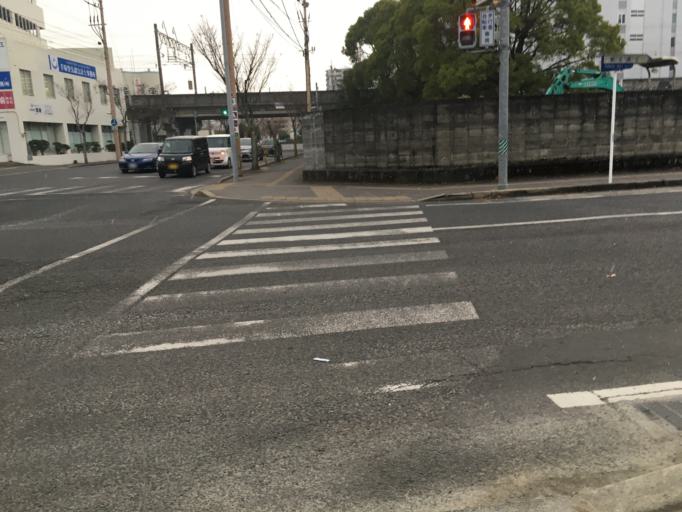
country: JP
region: Saga Prefecture
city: Saga-shi
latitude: 33.2658
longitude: 130.3019
